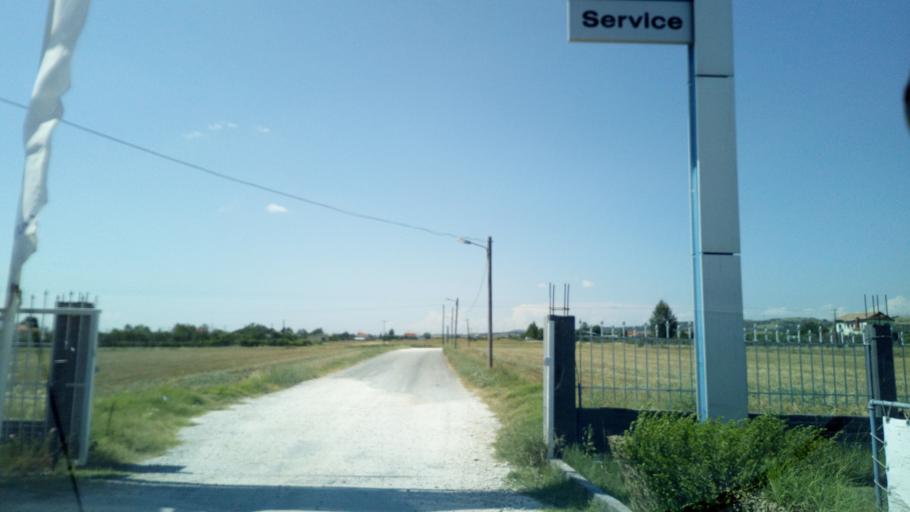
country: GR
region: Central Macedonia
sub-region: Nomos Thessalonikis
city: Lagkadas
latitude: 40.7668
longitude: 23.0865
